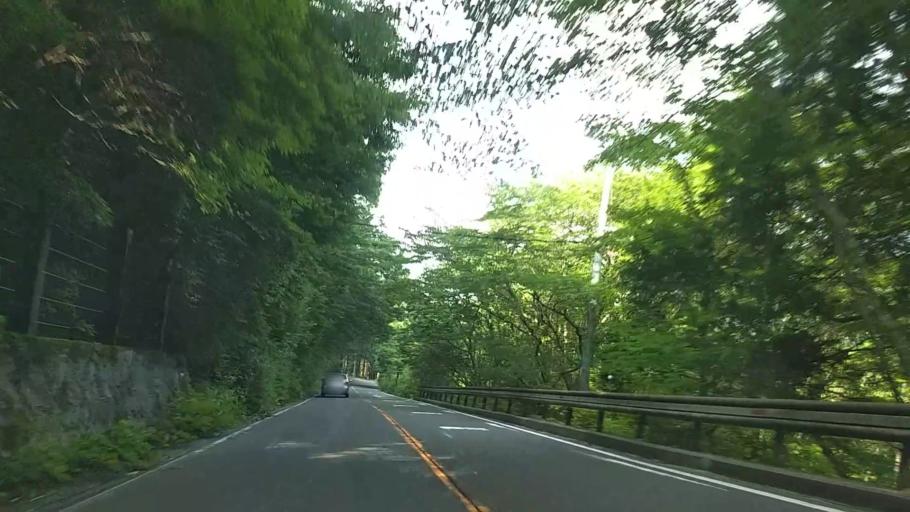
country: JP
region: Kanagawa
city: Hakone
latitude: 35.2250
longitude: 139.0480
